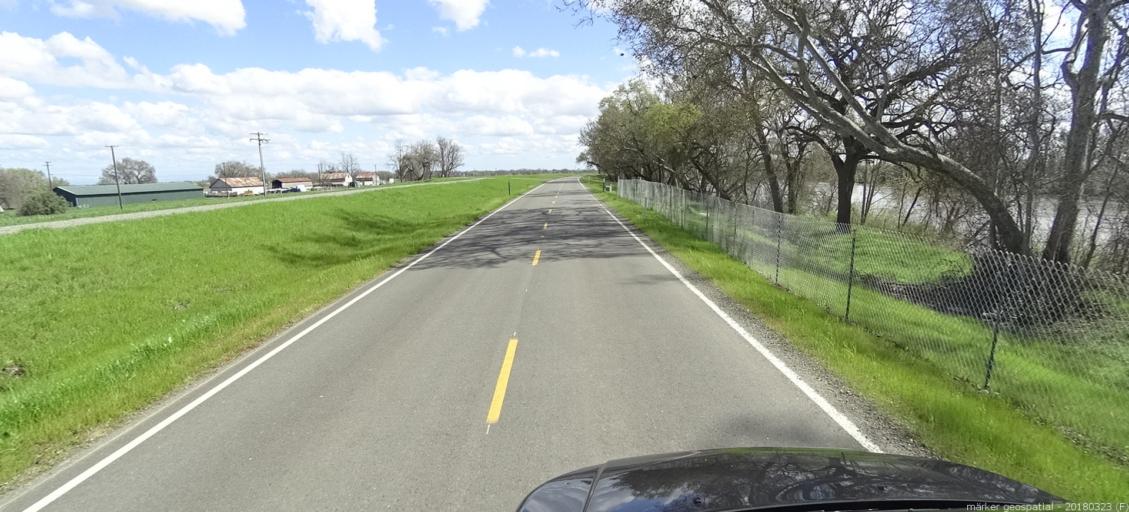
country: US
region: California
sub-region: Yolo County
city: West Sacramento
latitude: 38.6660
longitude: -121.6137
